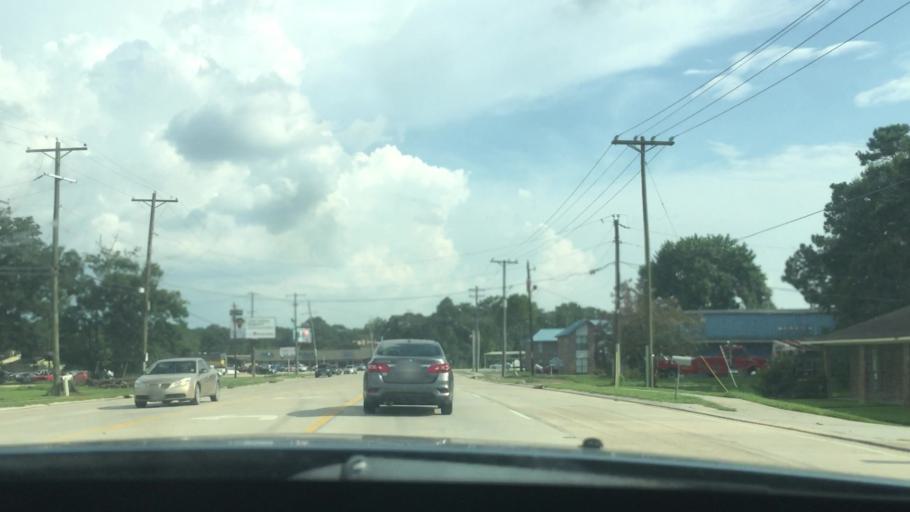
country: US
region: Louisiana
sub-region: East Baton Rouge Parish
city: Shenandoah
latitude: 30.4316
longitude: -91.0245
